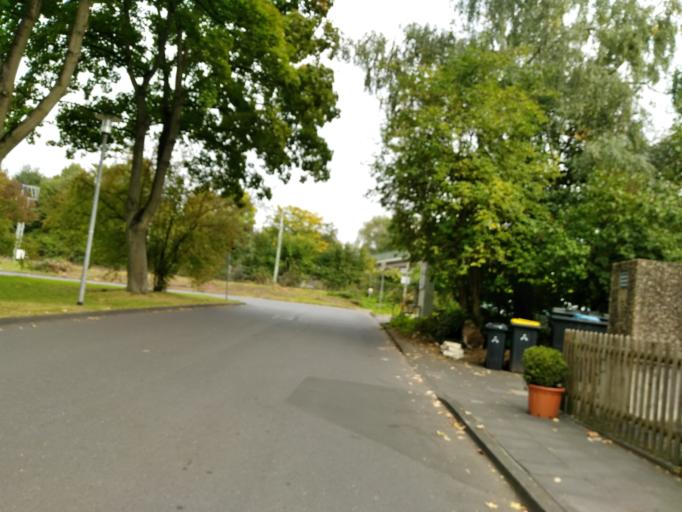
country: DE
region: North Rhine-Westphalia
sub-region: Regierungsbezirk Koln
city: Bad Honnef
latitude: 50.6436
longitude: 7.2175
